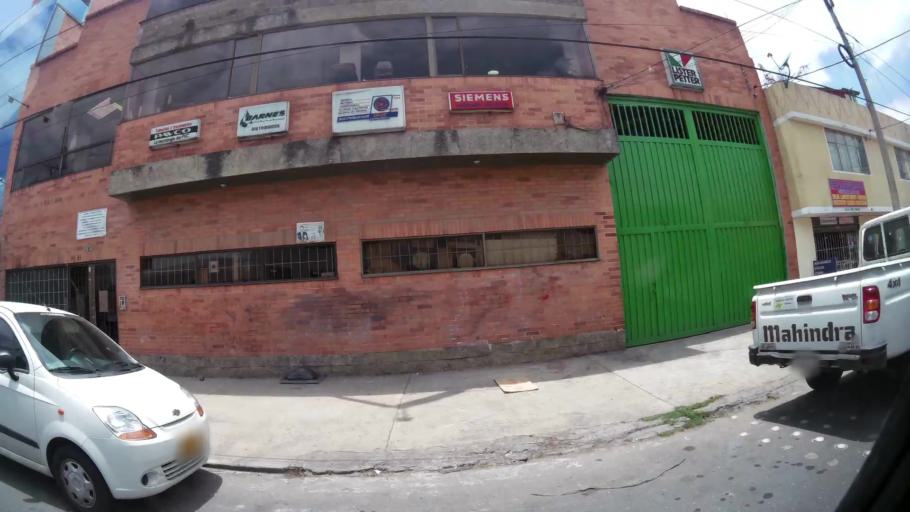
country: CO
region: Bogota D.C.
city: Barrio San Luis
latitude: 4.7186
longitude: -74.0569
